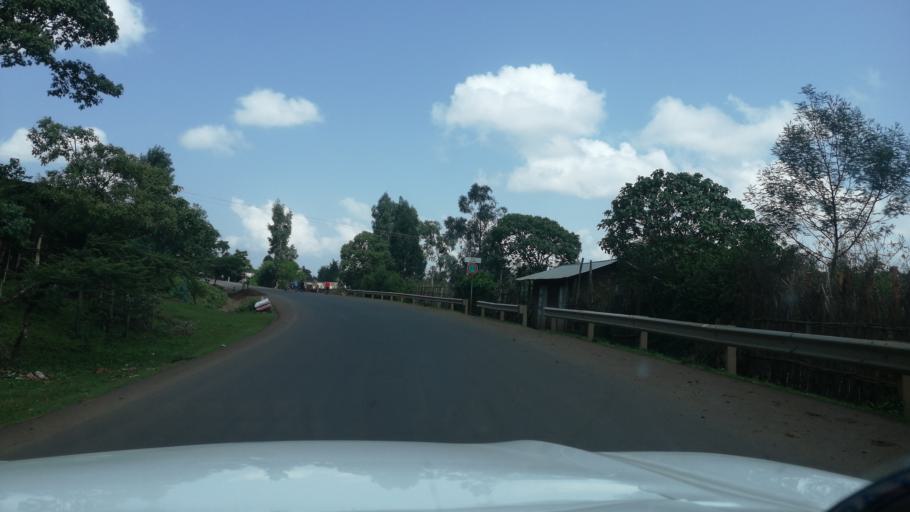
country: ET
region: Oromiya
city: Gedo
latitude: 8.9820
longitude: 37.5969
